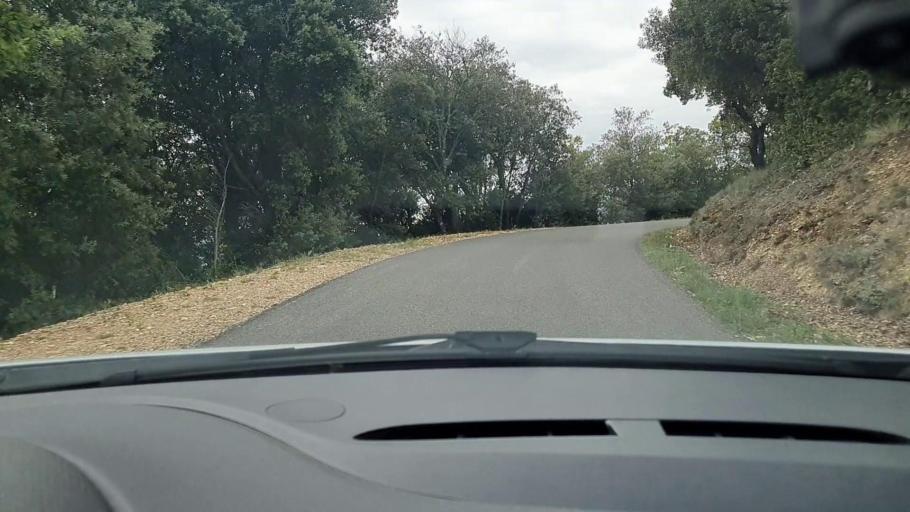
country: FR
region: Languedoc-Roussillon
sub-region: Departement du Gard
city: Mons
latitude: 44.1425
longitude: 4.2896
